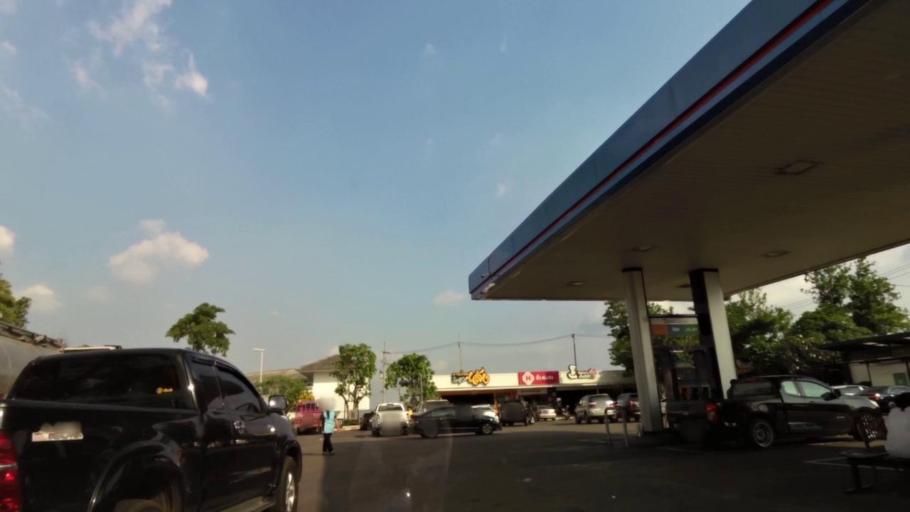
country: TH
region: Phra Nakhon Si Ayutthaya
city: Phra Nakhon Si Ayutthaya
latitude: 14.3042
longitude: 100.6143
